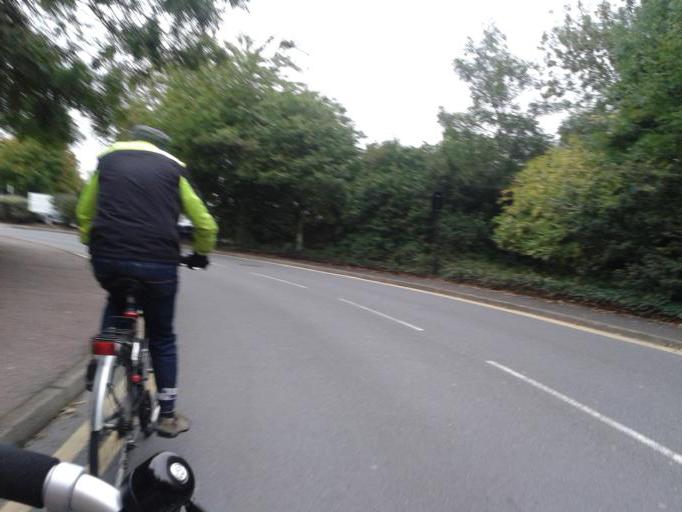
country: GB
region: England
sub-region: Leicestershire
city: Hinckley
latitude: 52.5543
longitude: -1.3804
